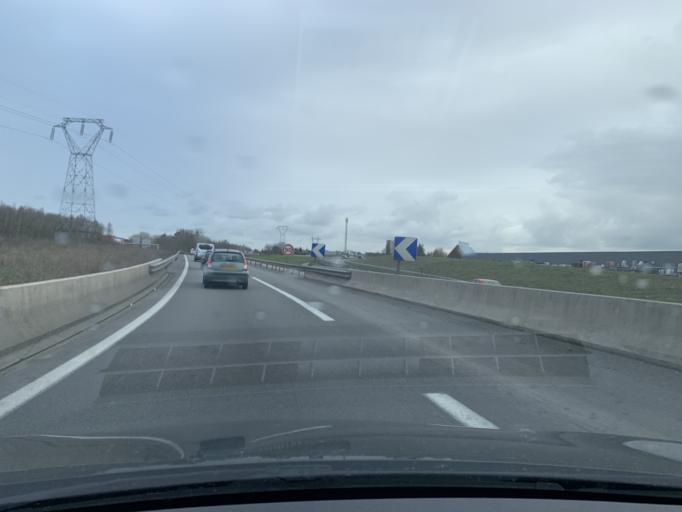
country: FR
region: Nord-Pas-de-Calais
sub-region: Departement du Nord
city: La Sentinelle
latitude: 50.3425
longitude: 3.4860
